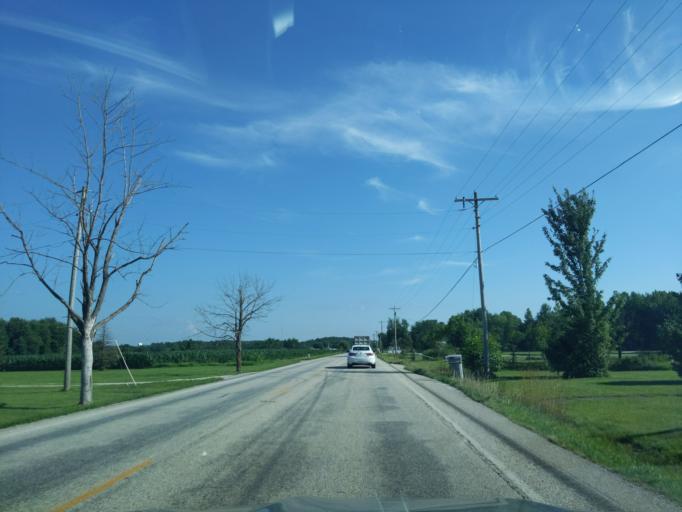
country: US
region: Indiana
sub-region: Ripley County
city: Versailles
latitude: 39.0812
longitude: -85.2729
